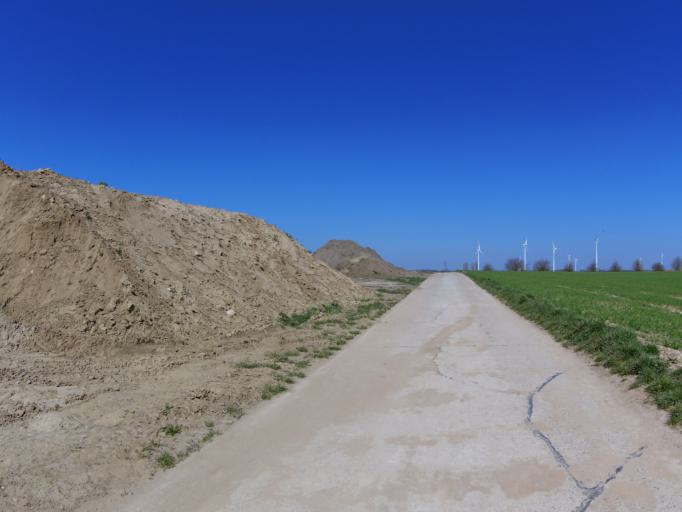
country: DE
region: Bavaria
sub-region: Regierungsbezirk Unterfranken
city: Biebelried
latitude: 49.7378
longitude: 10.0937
